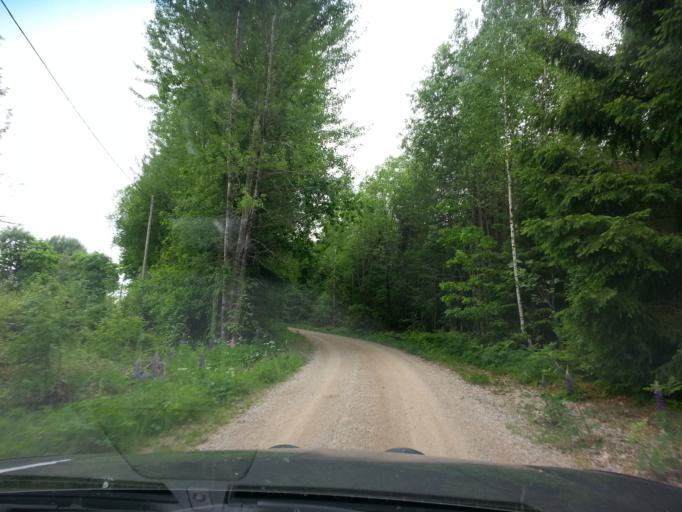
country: SE
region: Joenkoeping
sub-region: Vetlanda Kommun
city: Vetlanda
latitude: 57.2874
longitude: 15.1287
